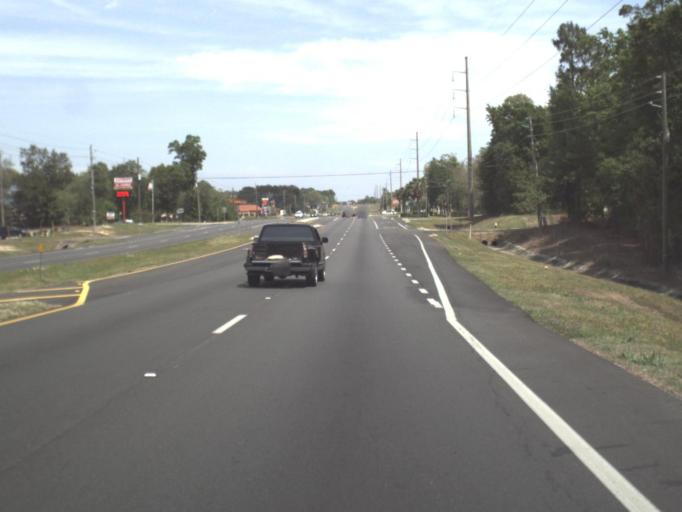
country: US
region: Florida
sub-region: Escambia County
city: Ferry Pass
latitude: 30.5323
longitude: -87.2307
